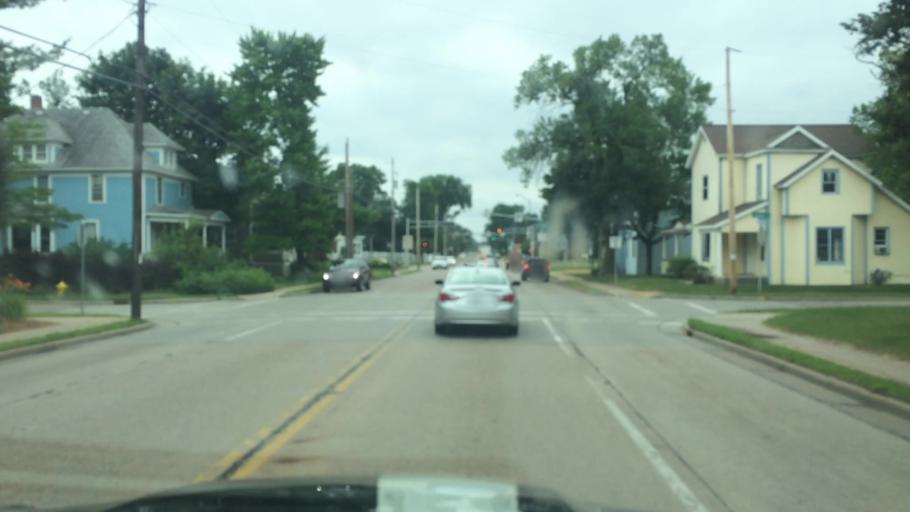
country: US
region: Wisconsin
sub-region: Portage County
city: Stevens Point
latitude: 44.5247
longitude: -89.5749
